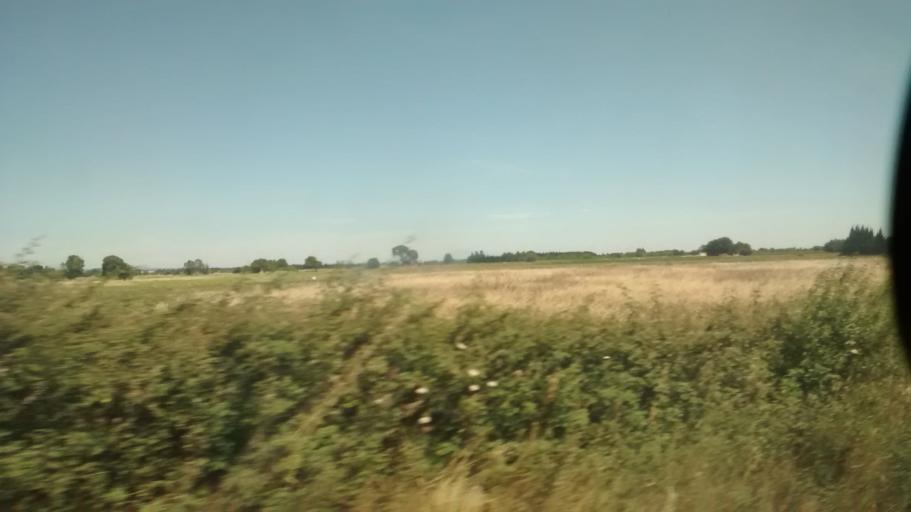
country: FR
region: Languedoc-Roussillon
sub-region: Departement du Gard
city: Manduel
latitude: 43.8327
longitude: 4.4572
